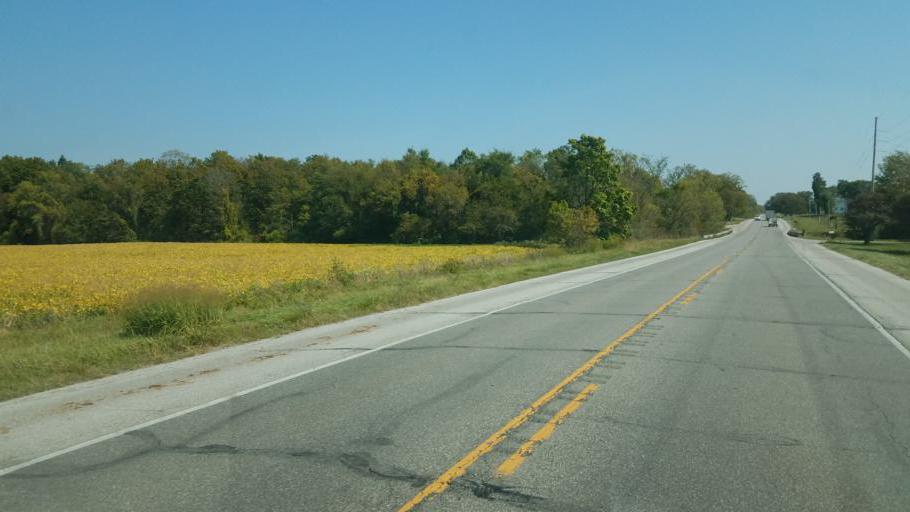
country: US
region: Indiana
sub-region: LaGrange County
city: Lagrange
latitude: 41.6419
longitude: -85.3411
